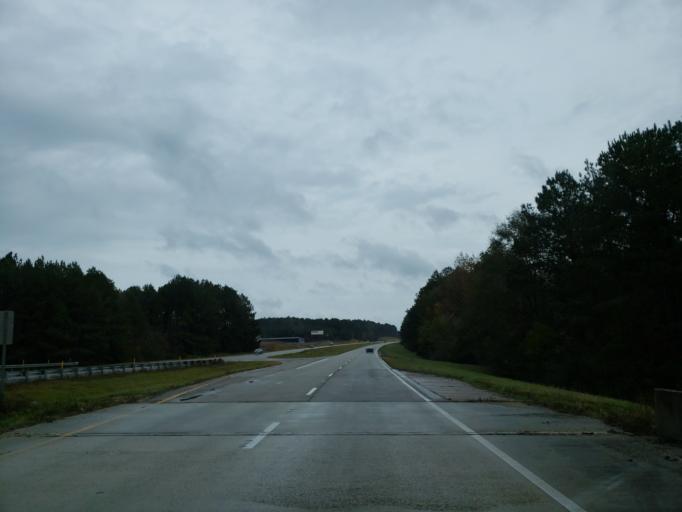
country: US
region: Mississippi
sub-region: Jones County
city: Laurel
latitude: 31.7053
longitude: -89.0730
